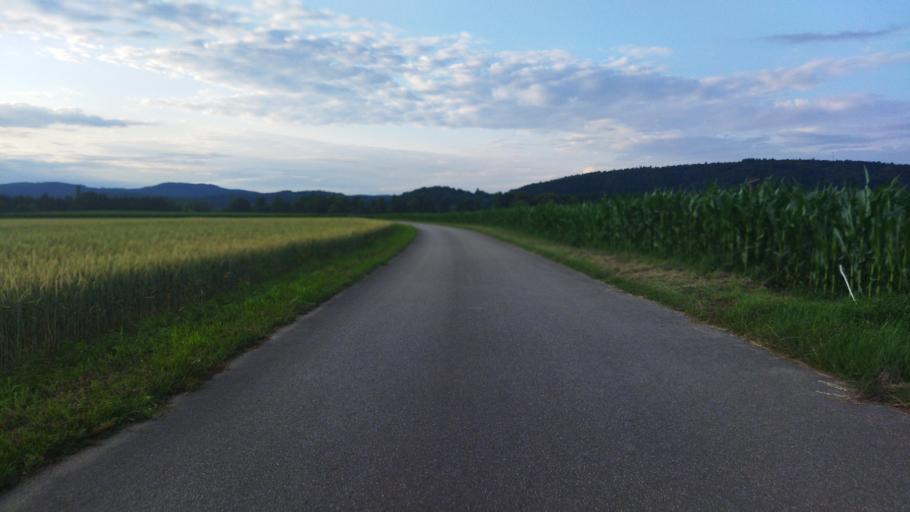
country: DE
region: Bavaria
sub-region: Upper Palatinate
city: Wiesent
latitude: 48.9907
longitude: 12.3813
